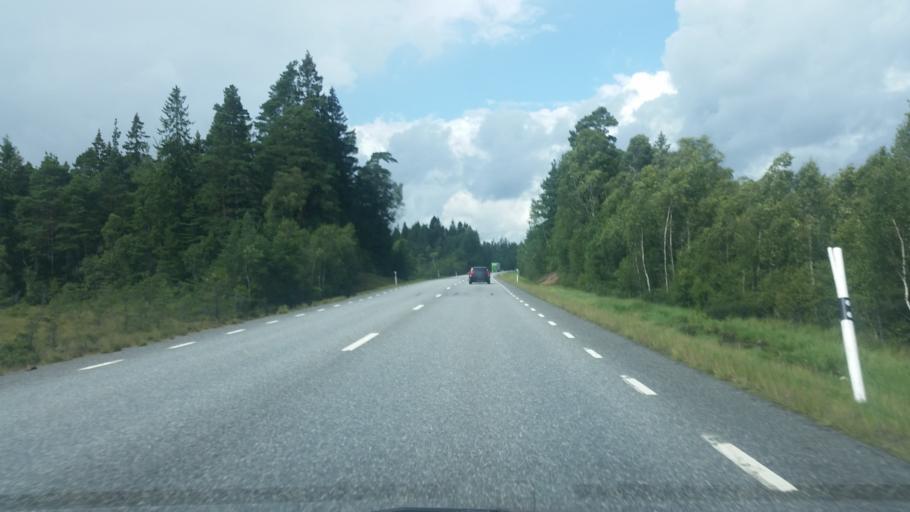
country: SE
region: Vaestra Goetaland
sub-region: Tranemo Kommun
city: Langhem
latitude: 57.5916
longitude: 13.1977
